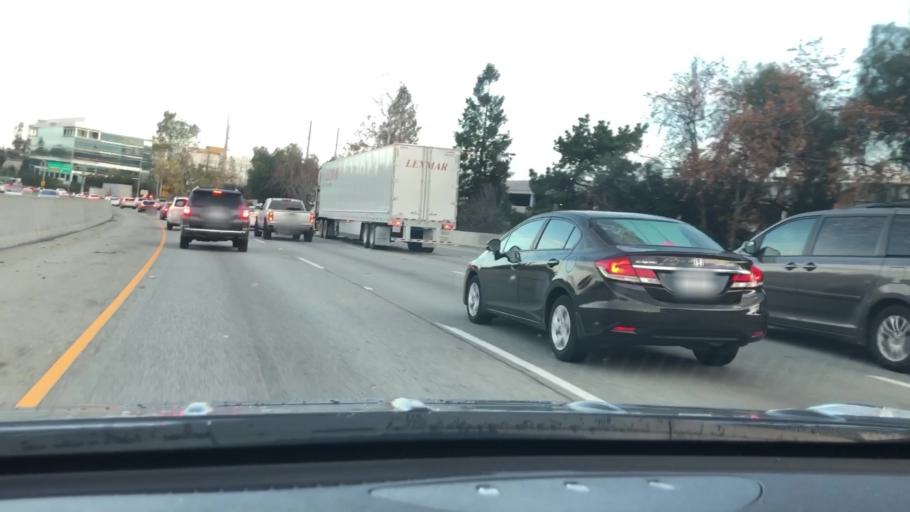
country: US
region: California
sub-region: Santa Clara County
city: Campbell
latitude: 37.2890
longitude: -121.9359
